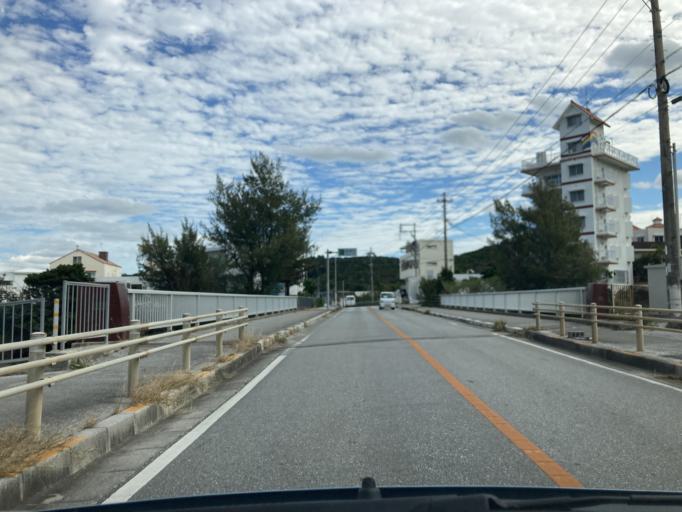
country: JP
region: Okinawa
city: Ishikawa
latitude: 26.4223
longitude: 127.7415
